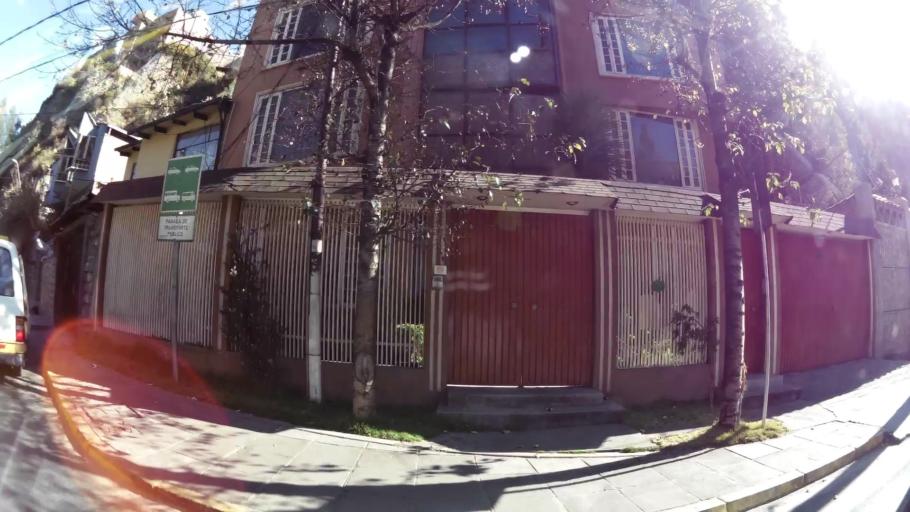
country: BO
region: La Paz
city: La Paz
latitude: -16.5124
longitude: -68.1197
